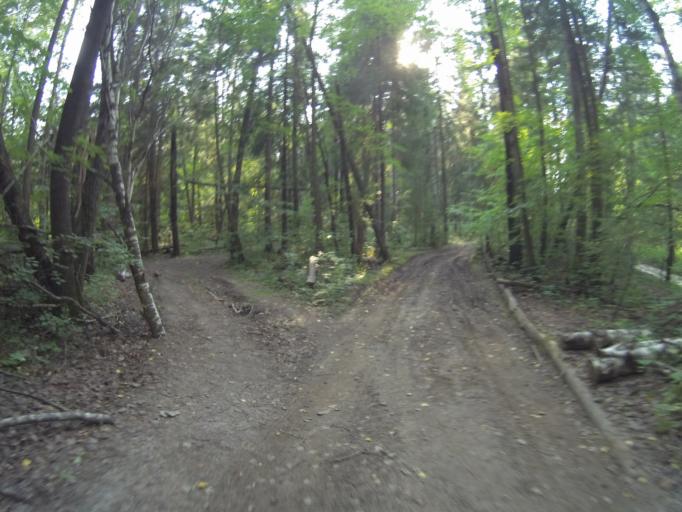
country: RU
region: Vladimir
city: Kommunar
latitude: 56.0489
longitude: 40.5680
